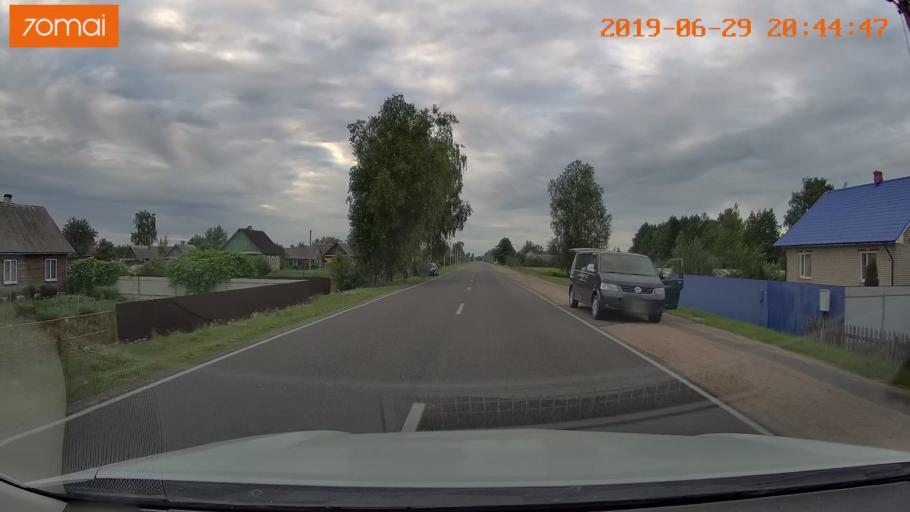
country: BY
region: Brest
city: Hantsavichy
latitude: 52.6170
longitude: 26.3074
